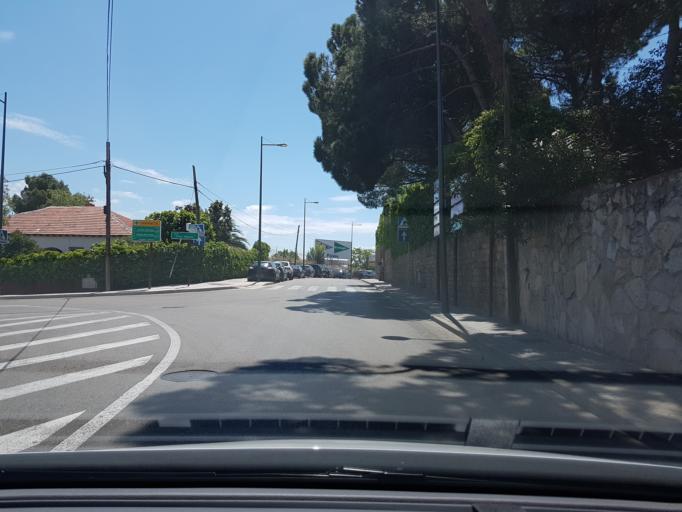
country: ES
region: Madrid
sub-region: Provincia de Madrid
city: Pozuelo de Alarcon
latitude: 40.4332
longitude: -3.8120
